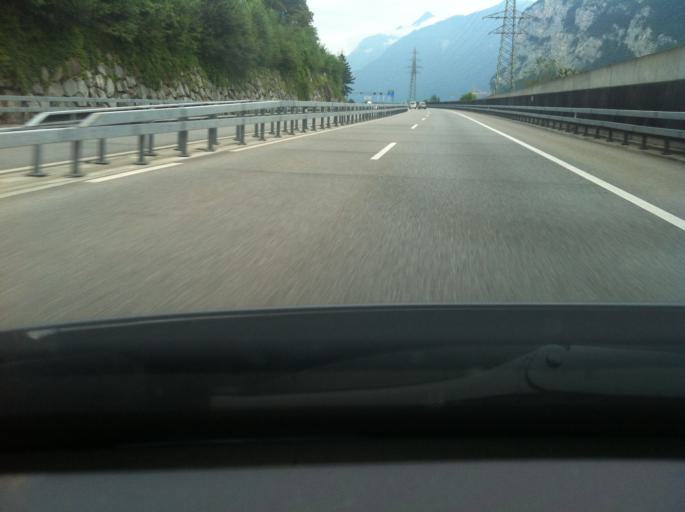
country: CH
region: Uri
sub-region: Uri
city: Erstfeld
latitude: 46.8215
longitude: 8.6416
